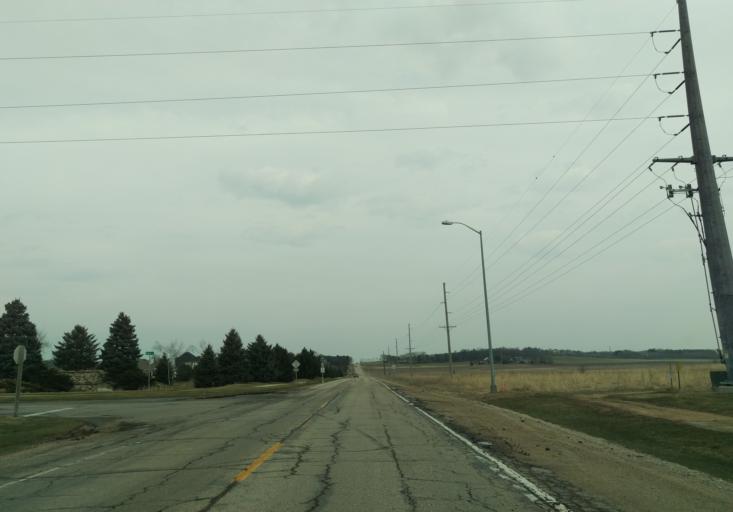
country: US
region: Wisconsin
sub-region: Dane County
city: Waunakee
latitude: 43.2026
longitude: -89.4617
